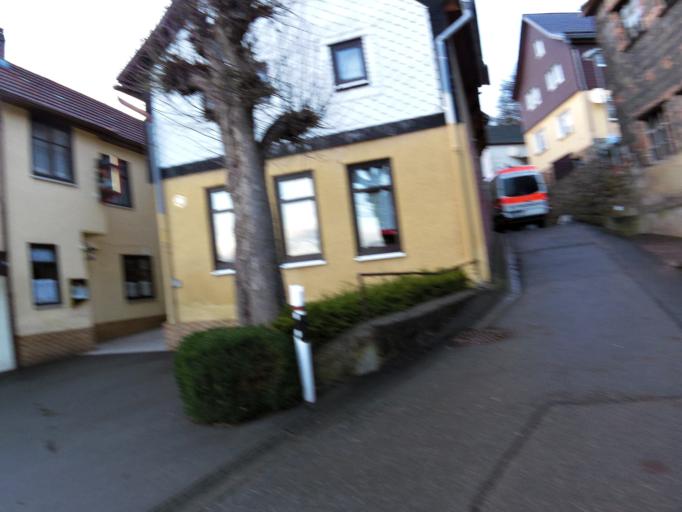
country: DE
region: Thuringia
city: Steinbach
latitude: 50.8349
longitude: 10.3639
